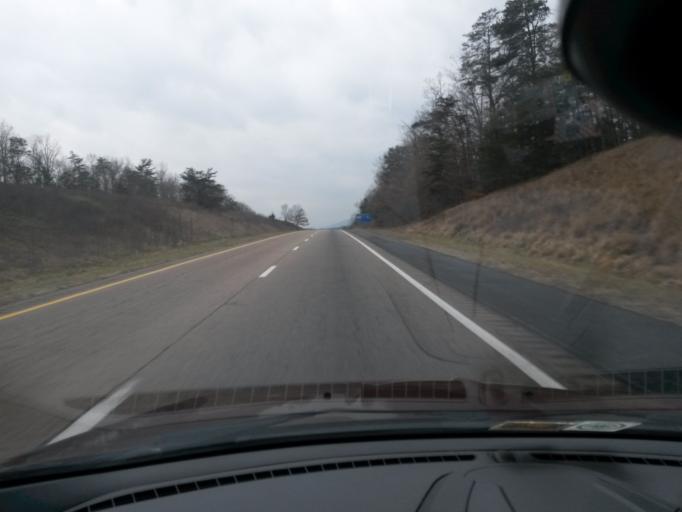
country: US
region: Virginia
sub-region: Alleghany County
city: Clifton Forge
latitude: 37.8300
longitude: -79.7736
